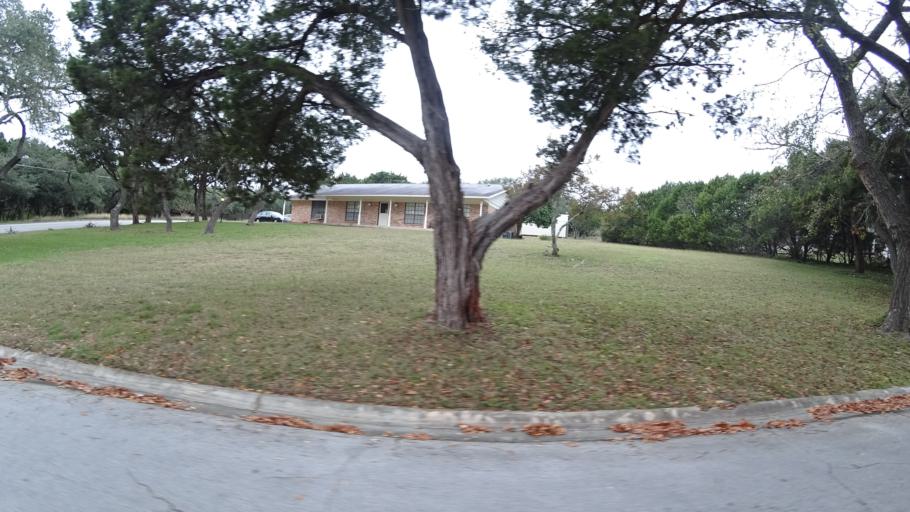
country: US
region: Texas
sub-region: Travis County
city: Shady Hollow
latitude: 30.2217
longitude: -97.9029
